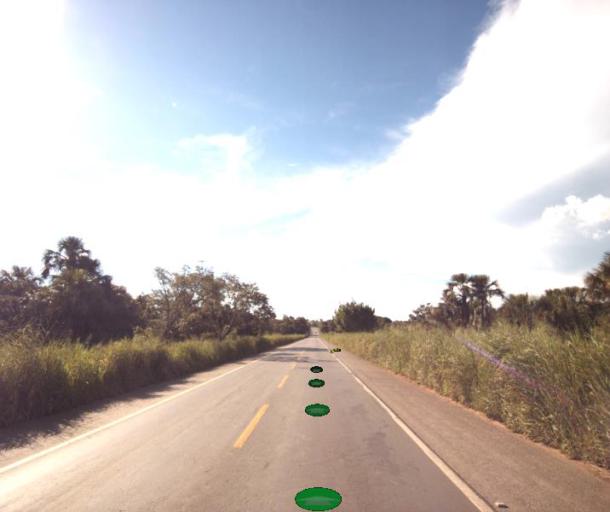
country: BR
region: Goias
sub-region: Rialma
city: Rialma
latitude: -15.4344
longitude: -49.5108
